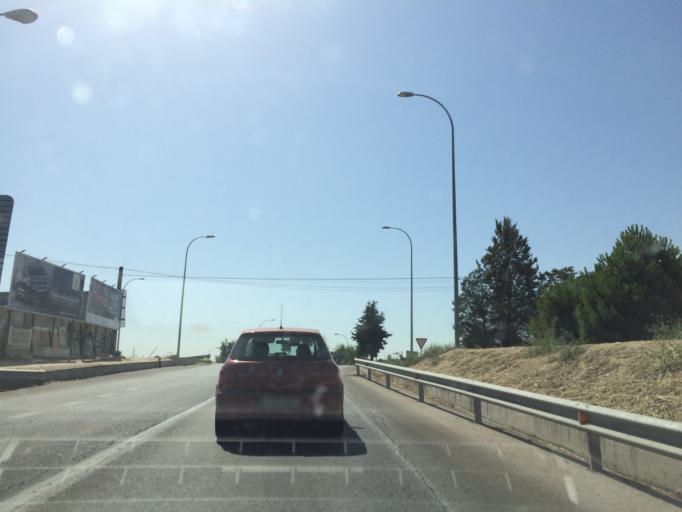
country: ES
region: Madrid
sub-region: Provincia de Madrid
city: Pozuelo de Alarcon
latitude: 40.4353
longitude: -3.8325
